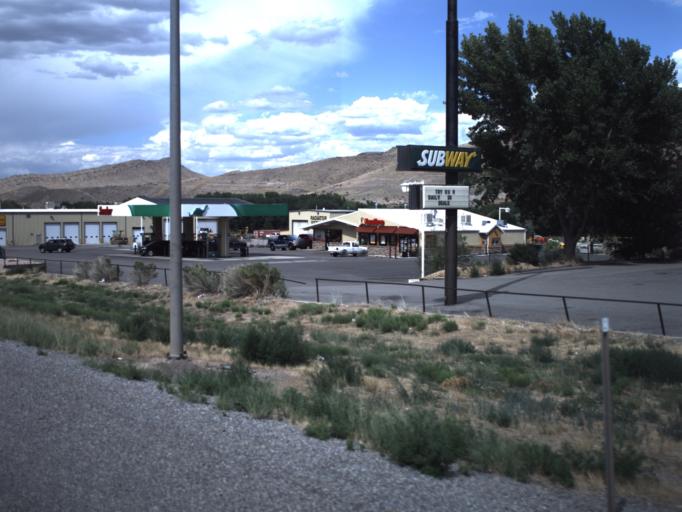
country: US
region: Utah
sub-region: Sevier County
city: Salina
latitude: 38.9376
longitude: -111.8546
